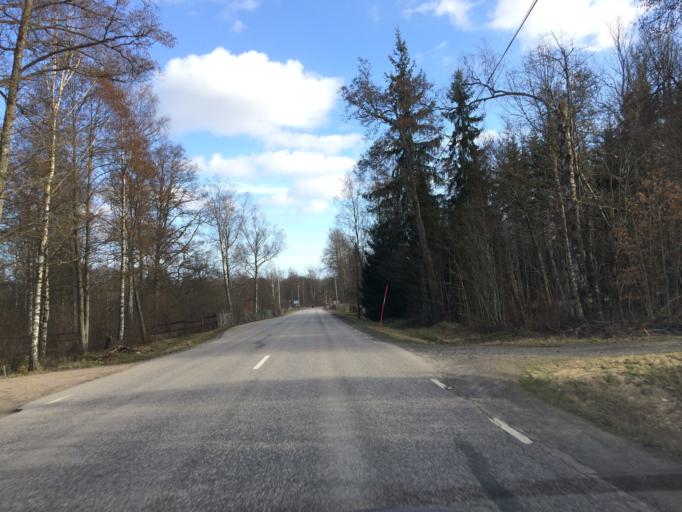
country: SE
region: Kronoberg
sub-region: Almhults Kommun
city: AElmhult
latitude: 56.5676
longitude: 14.1238
